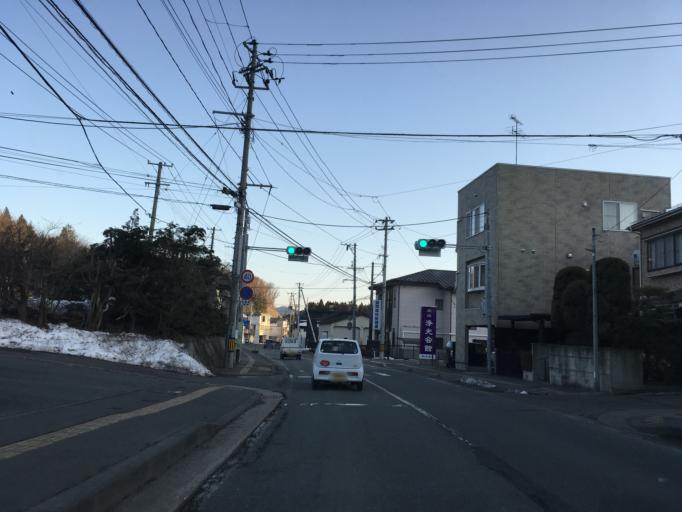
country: JP
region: Iwate
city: Morioka-shi
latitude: 39.7172
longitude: 141.1550
